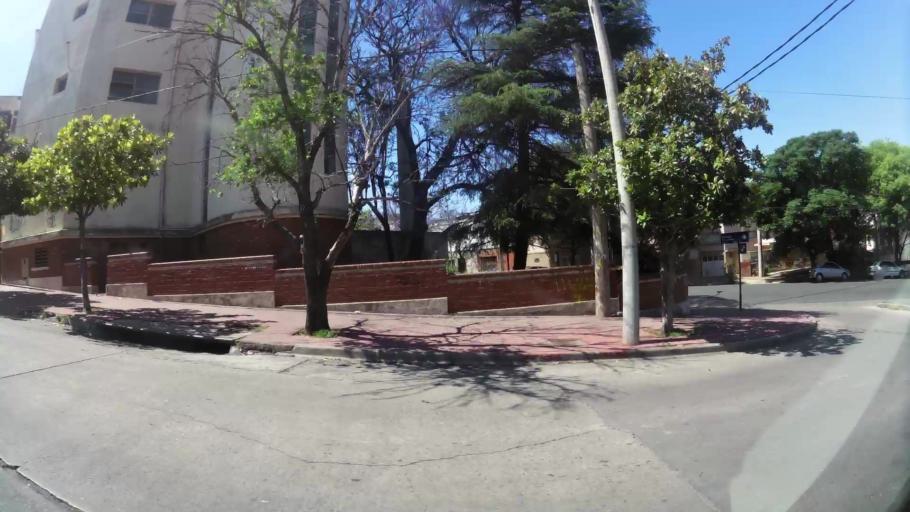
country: AR
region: Cordoba
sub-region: Departamento de Capital
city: Cordoba
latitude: -31.4028
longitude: -64.1831
